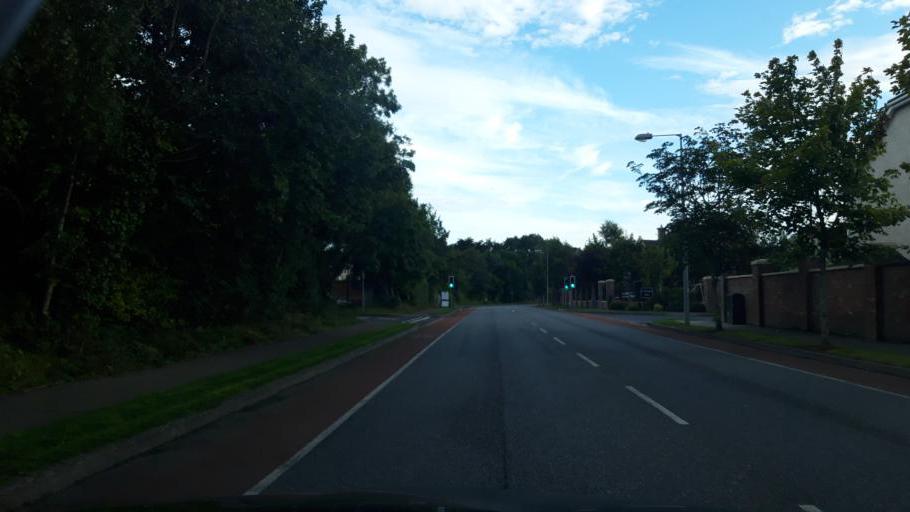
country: IE
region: Leinster
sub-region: Kildare
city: Celbridge
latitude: 53.3367
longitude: -6.5310
